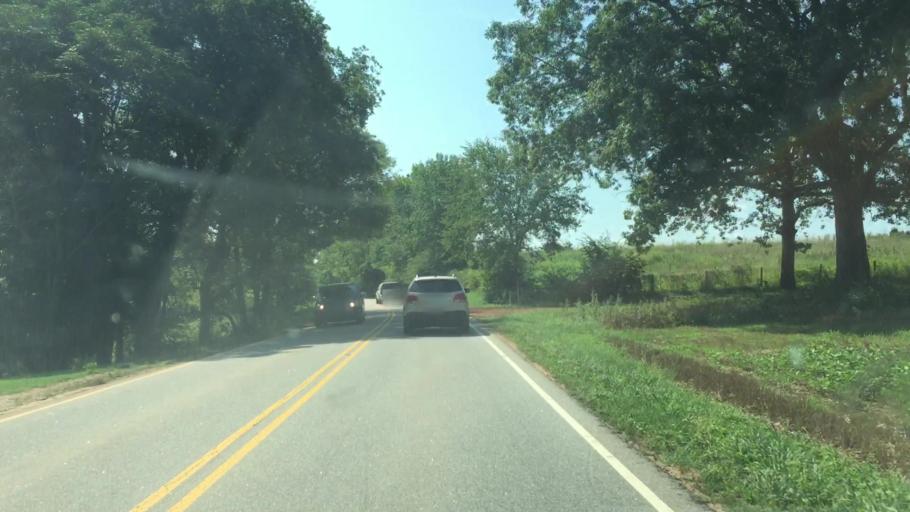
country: US
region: North Carolina
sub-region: Anson County
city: Burnsville
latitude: 35.0955
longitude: -80.3049
